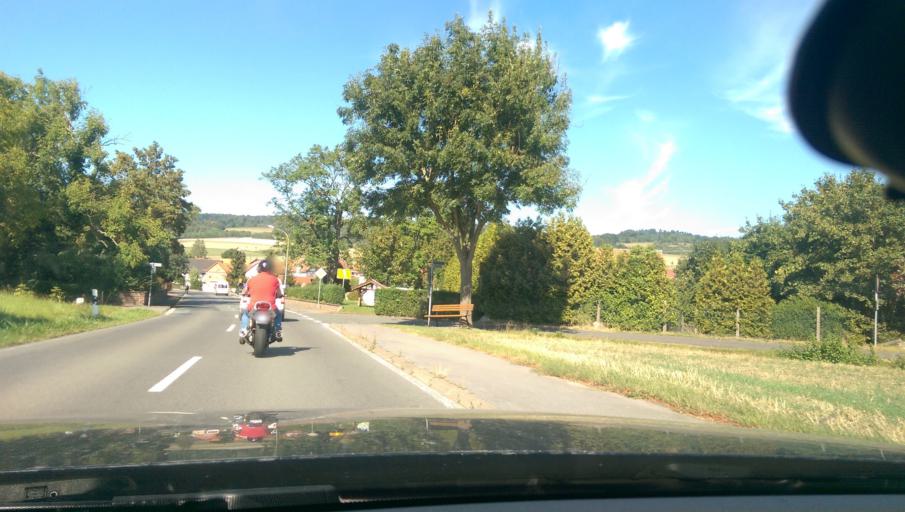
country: DE
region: Hesse
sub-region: Regierungsbezirk Kassel
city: Weissenborn
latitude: 51.0906
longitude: 10.0944
